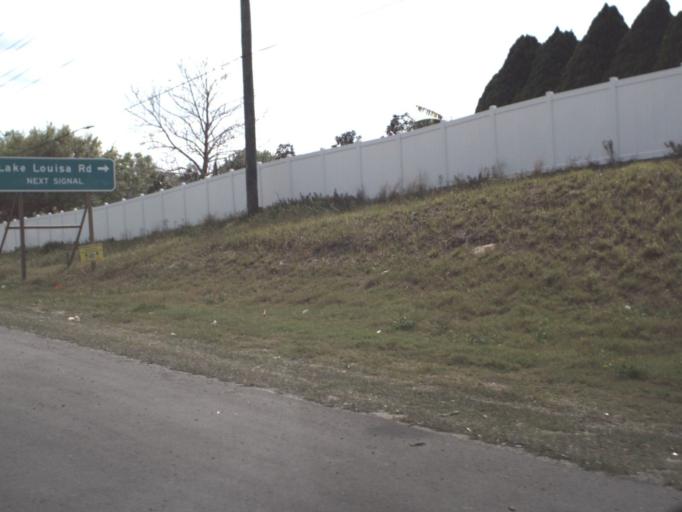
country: US
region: Florida
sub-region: Lake County
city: Clermont
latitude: 28.4881
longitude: -81.7153
